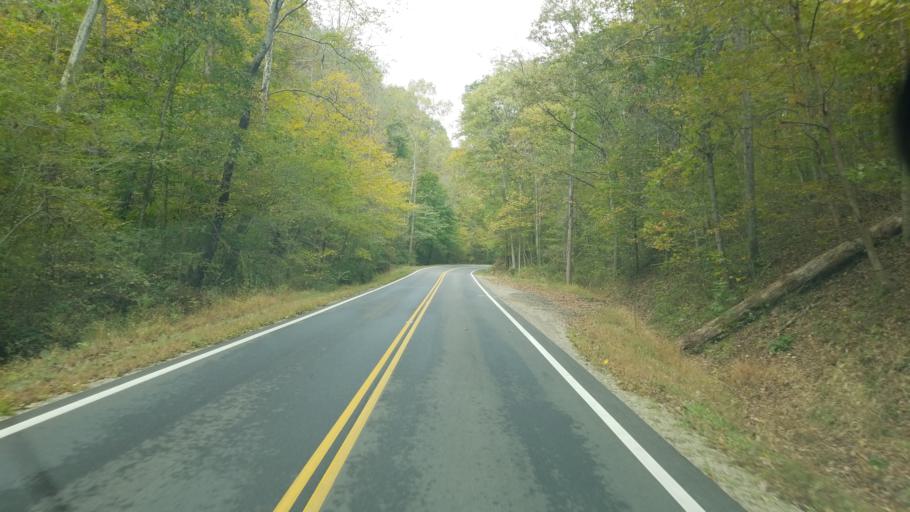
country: US
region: Ohio
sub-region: Jackson County
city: Wellston
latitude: 39.1574
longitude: -82.6167
